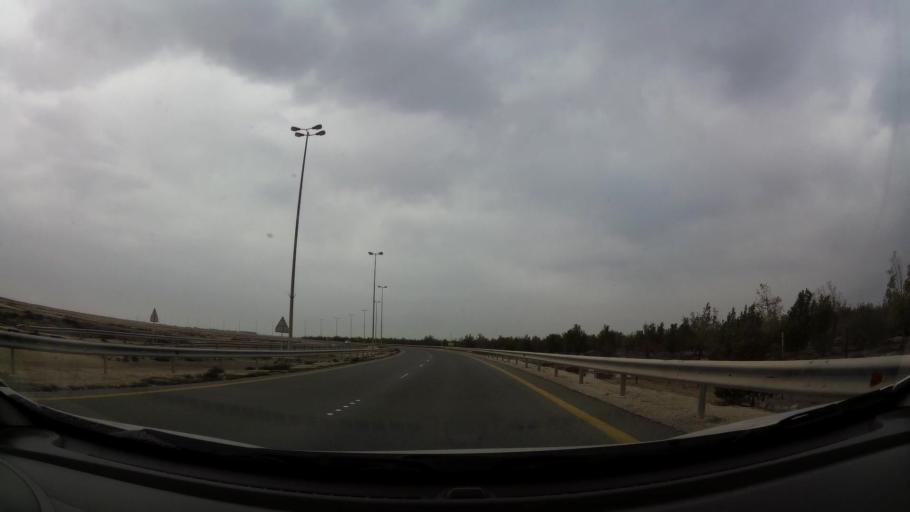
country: BH
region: Central Governorate
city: Dar Kulayb
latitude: 26.0154
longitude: 50.4850
